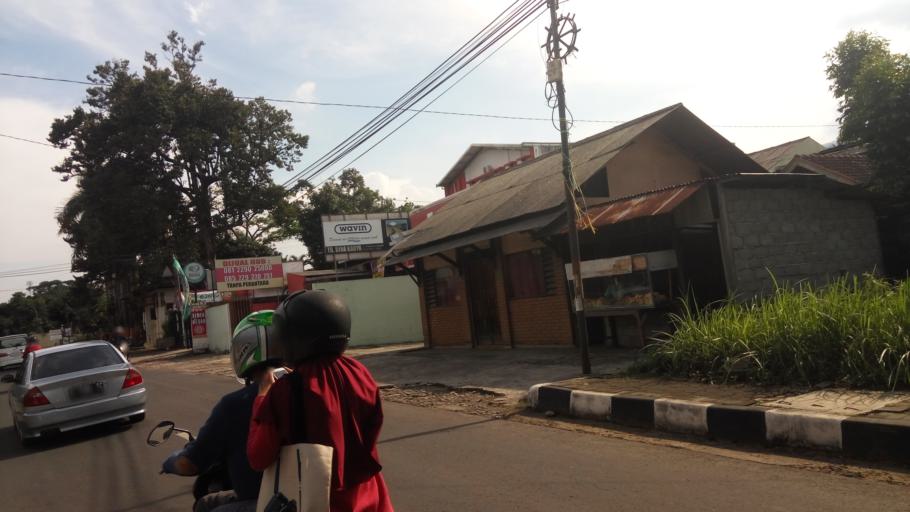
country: ID
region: Central Java
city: Ungaran
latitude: -7.1387
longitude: 110.4114
